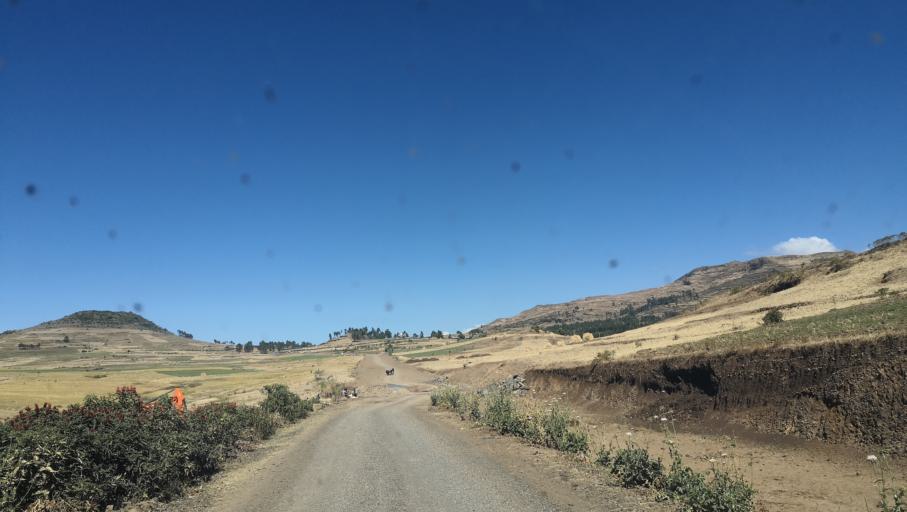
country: ET
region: Amhara
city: Debre Tabor
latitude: 11.5601
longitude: 38.1406
